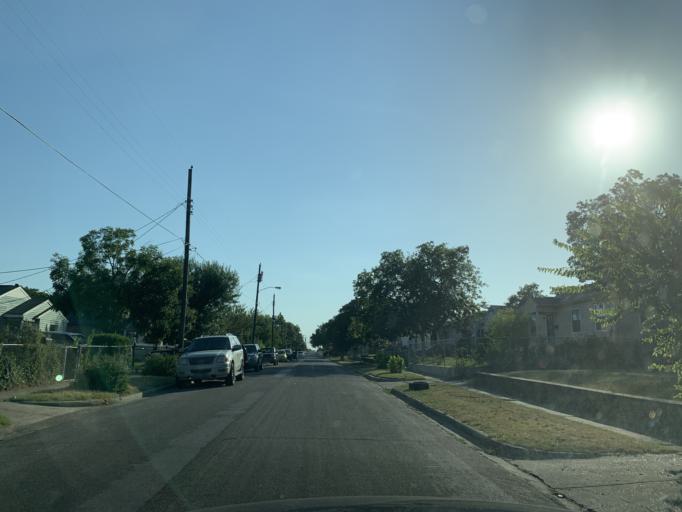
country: US
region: Texas
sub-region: Dallas County
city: Dallas
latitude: 32.7093
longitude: -96.7939
